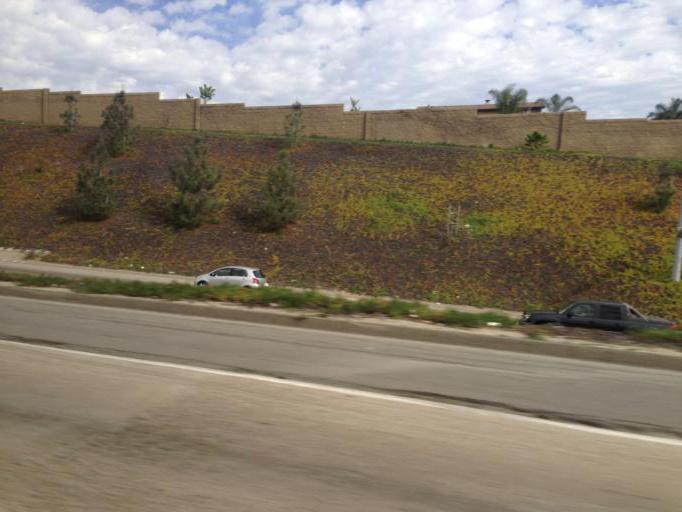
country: US
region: California
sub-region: San Diego County
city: Bonita
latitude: 32.5964
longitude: -117.0362
